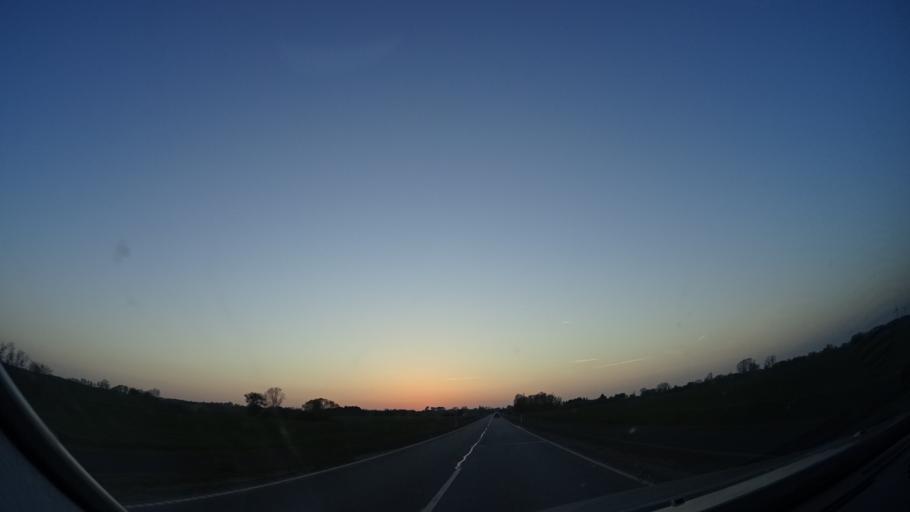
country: DK
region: Zealand
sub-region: Lejre Kommune
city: Ejby
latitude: 55.6641
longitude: 11.8995
